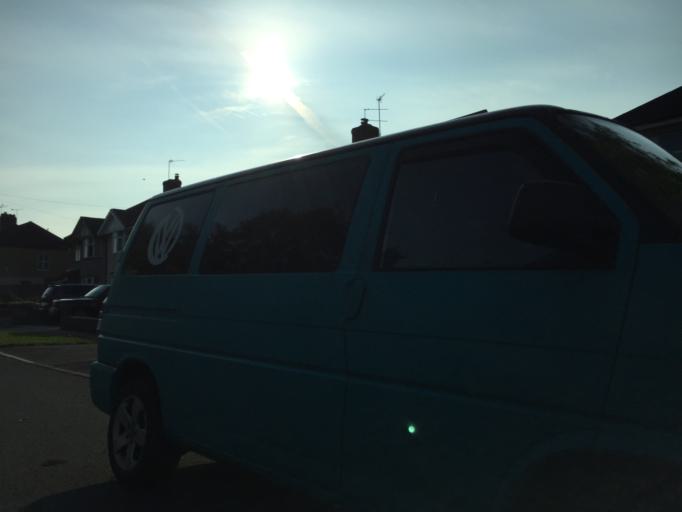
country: GB
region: England
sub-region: South Gloucestershire
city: Stoke Gifford
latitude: 51.5043
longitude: -2.5841
